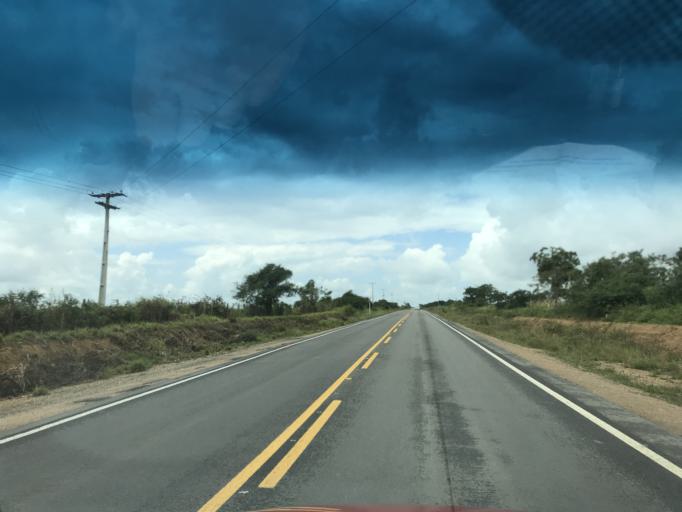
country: BR
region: Bahia
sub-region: Conceicao Do Almeida
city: Conceicao do Almeida
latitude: -12.6676
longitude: -39.2804
